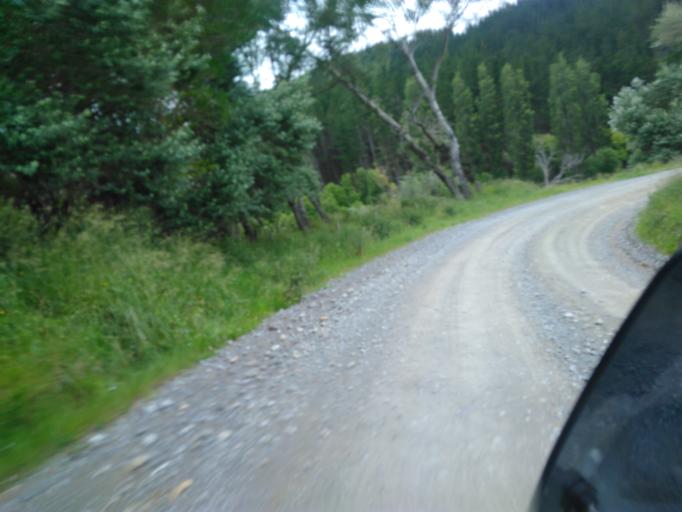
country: NZ
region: Gisborne
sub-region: Gisborne District
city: Gisborne
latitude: -38.0831
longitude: 178.0590
